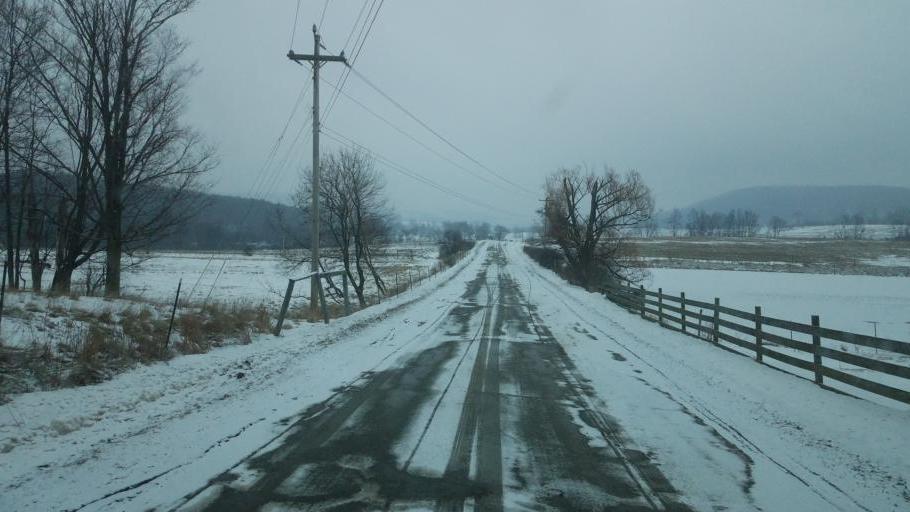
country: US
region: Pennsylvania
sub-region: Tioga County
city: Elkland
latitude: 42.1040
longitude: -77.4677
